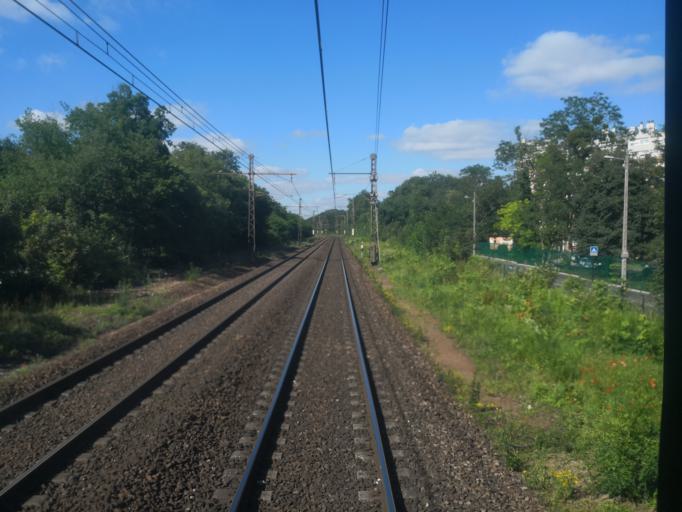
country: FR
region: Ile-de-France
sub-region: Departement de Seine-et-Marne
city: Avon
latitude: 48.4216
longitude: 2.7308
